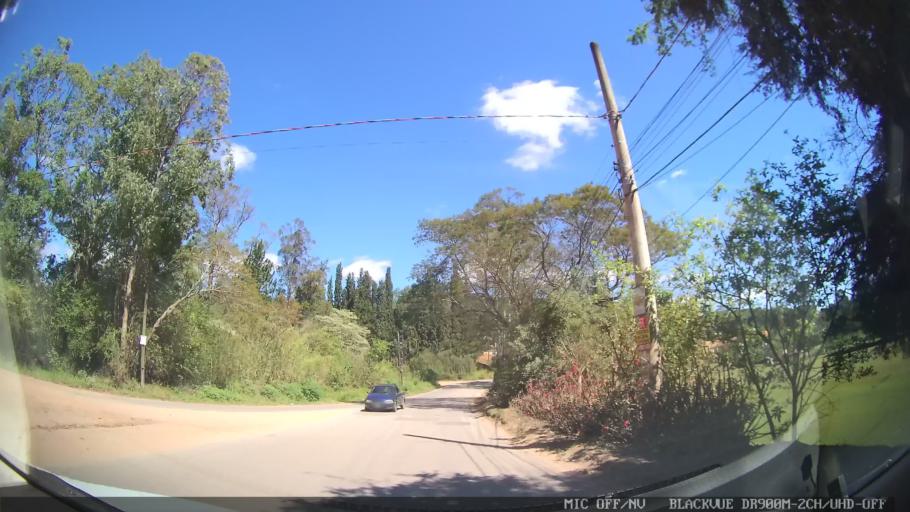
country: BR
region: Sao Paulo
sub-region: Campo Limpo Paulista
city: Campo Limpo Paulista
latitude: -23.1804
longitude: -46.7496
